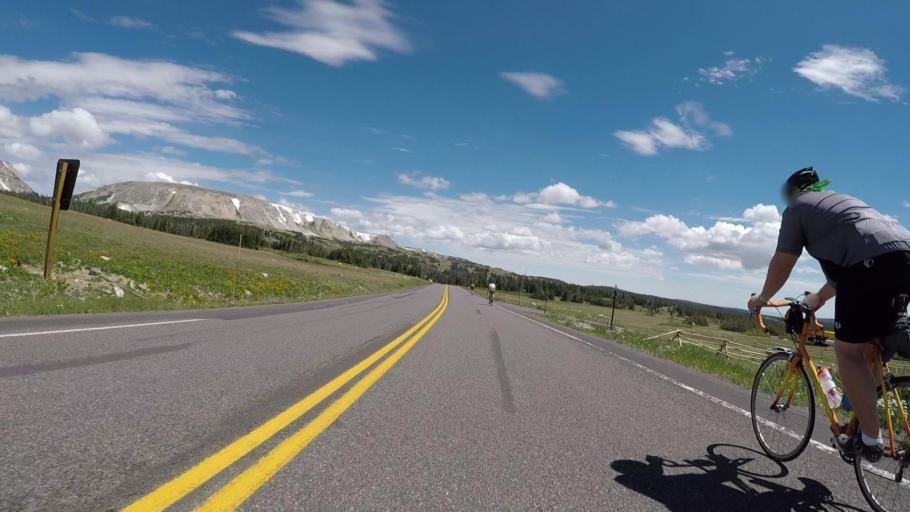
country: US
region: Wyoming
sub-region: Carbon County
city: Saratoga
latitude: 41.3454
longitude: -106.2919
